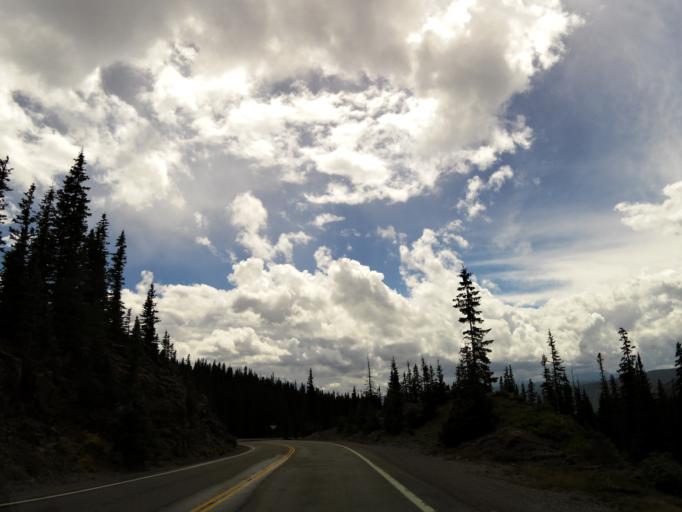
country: US
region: Colorado
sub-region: San Juan County
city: Silverton
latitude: 37.6961
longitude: -107.7765
